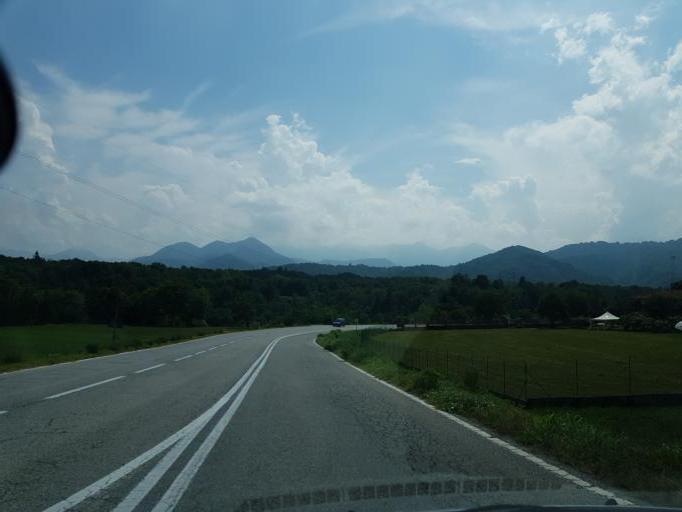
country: IT
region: Piedmont
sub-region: Provincia di Cuneo
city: Vignolo
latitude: 44.3492
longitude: 7.4763
